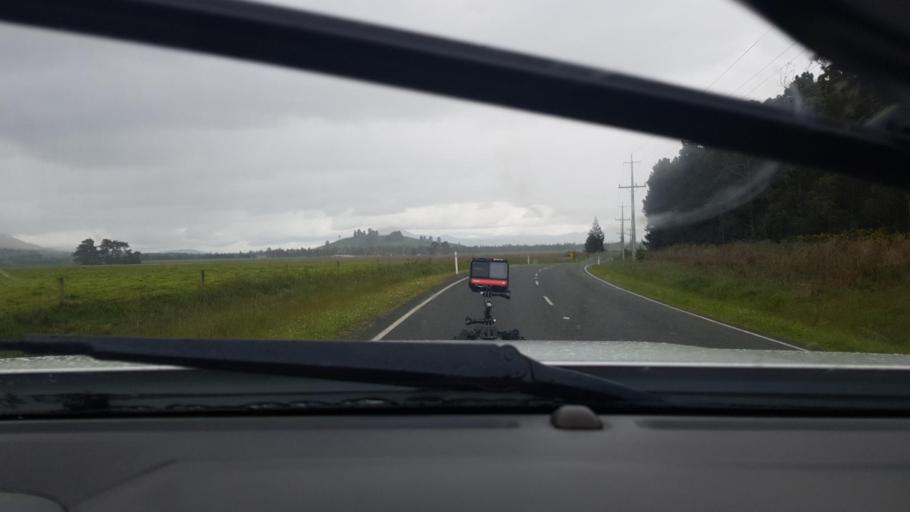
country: NZ
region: Southland
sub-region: Southland District
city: Winton
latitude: -45.7513
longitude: 168.4007
